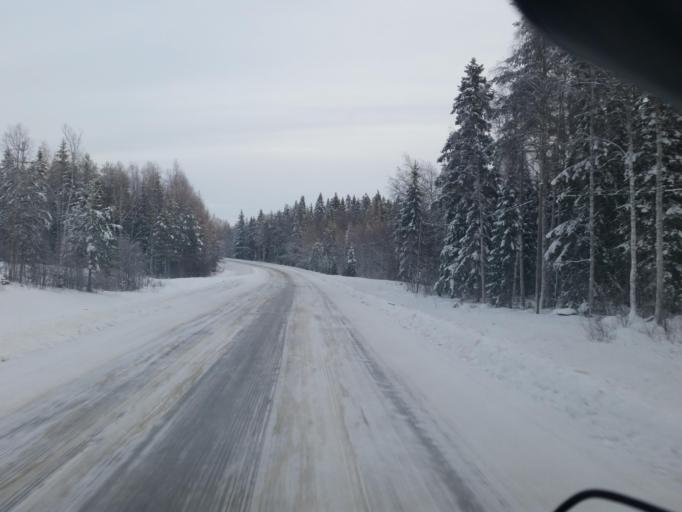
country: SE
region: Norrbotten
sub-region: Pitea Kommun
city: Rosvik
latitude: 65.4138
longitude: 21.7414
